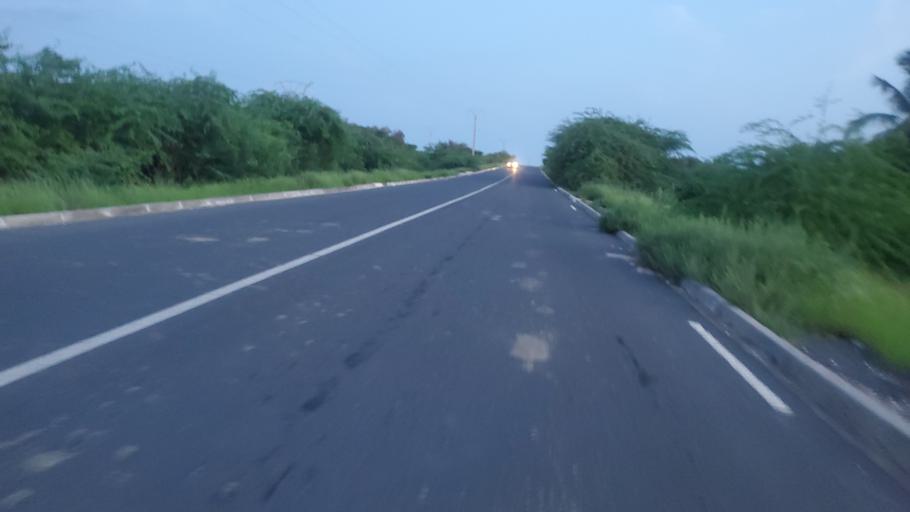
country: SN
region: Saint-Louis
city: Saint-Louis
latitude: 16.0784
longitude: -16.3907
